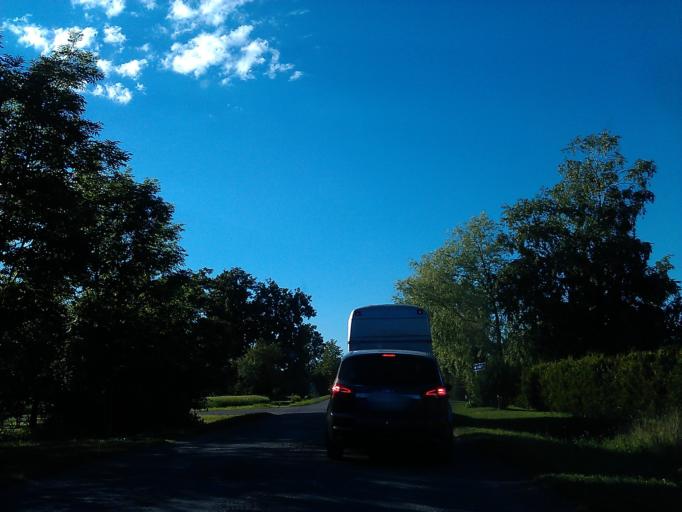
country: LV
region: Varaklani
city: Varaklani
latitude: 56.5789
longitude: 26.8005
